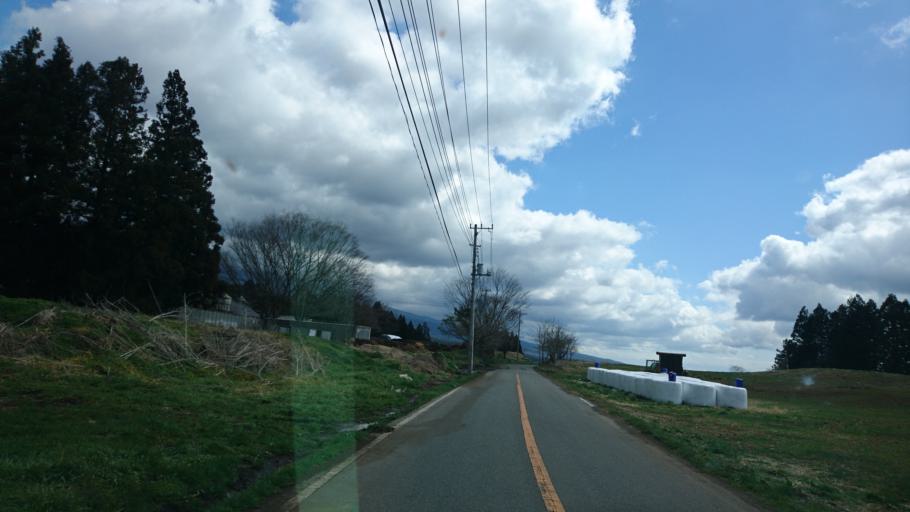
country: JP
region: Yamanashi
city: Fujikawaguchiko
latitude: 35.3783
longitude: 138.5978
